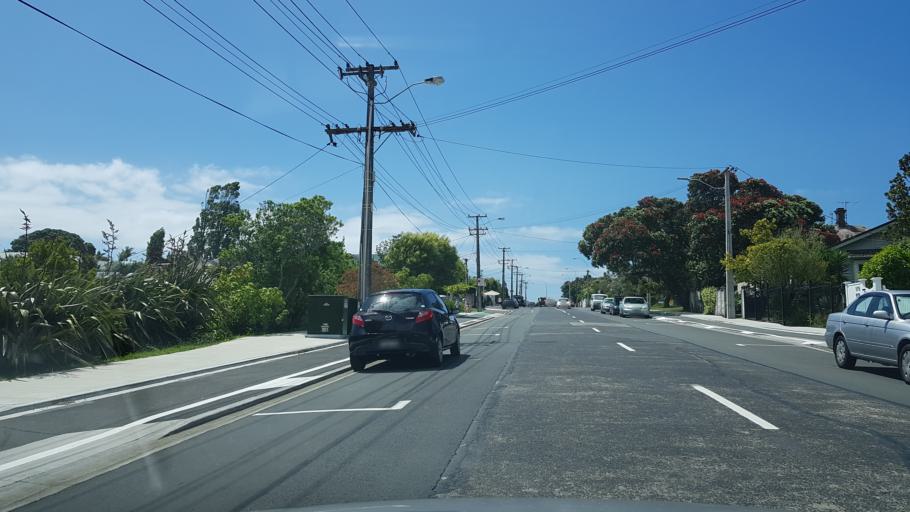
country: NZ
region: Auckland
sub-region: Auckland
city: North Shore
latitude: -36.8140
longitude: 174.7451
